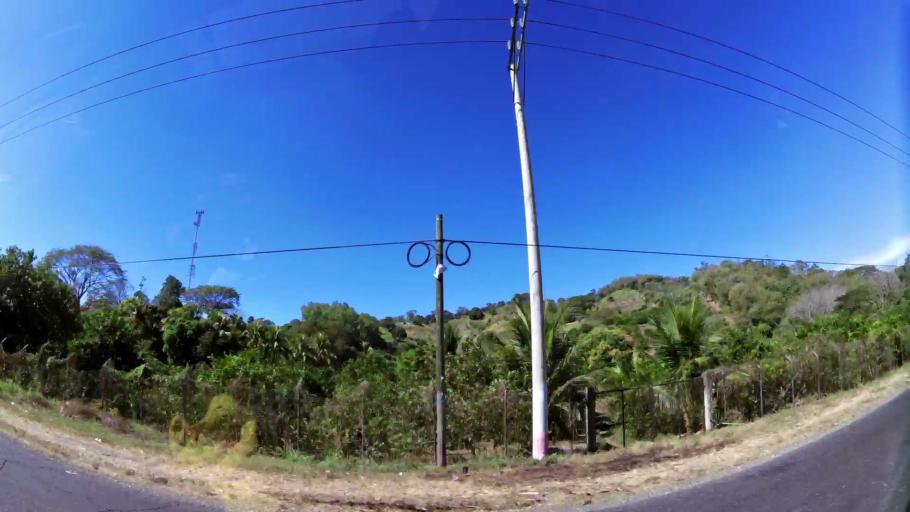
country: SV
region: La Libertad
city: San Juan Opico
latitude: 13.8360
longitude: -89.3592
